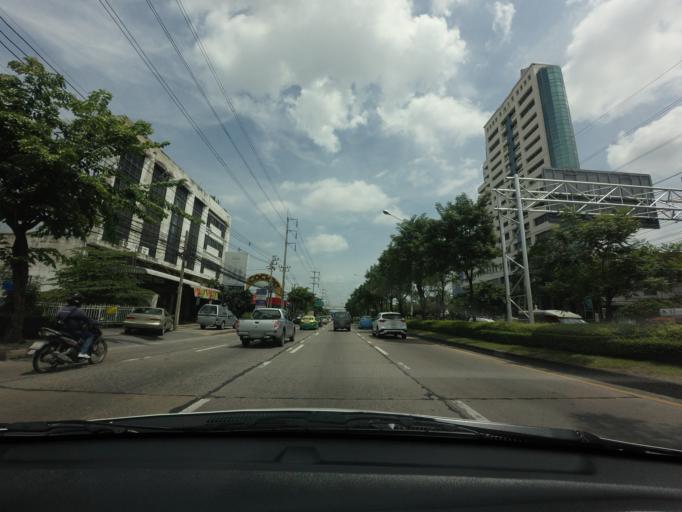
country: TH
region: Bangkok
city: Khan Na Yao
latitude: 13.8350
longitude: 100.6664
